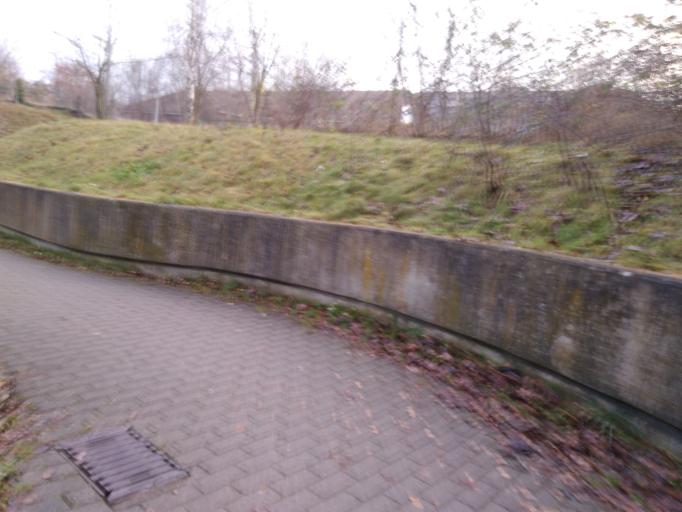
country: DE
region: Hamburg
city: Wandsbek
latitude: 53.5750
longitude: 10.0975
